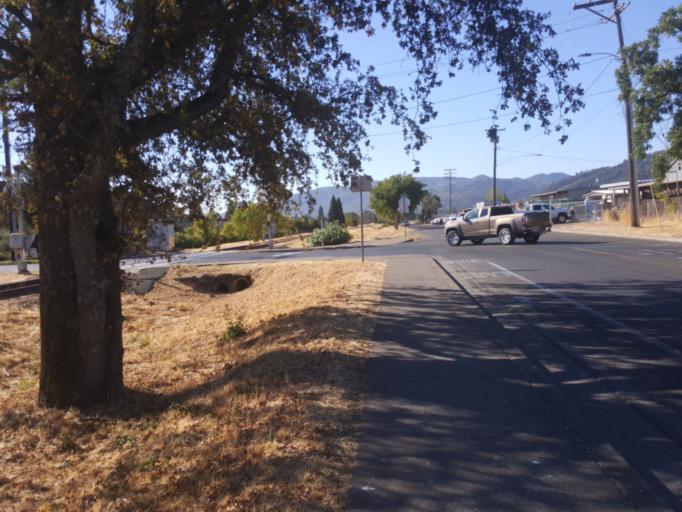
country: US
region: California
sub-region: Mendocino County
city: Ukiah
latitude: 39.1331
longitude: -123.2005
